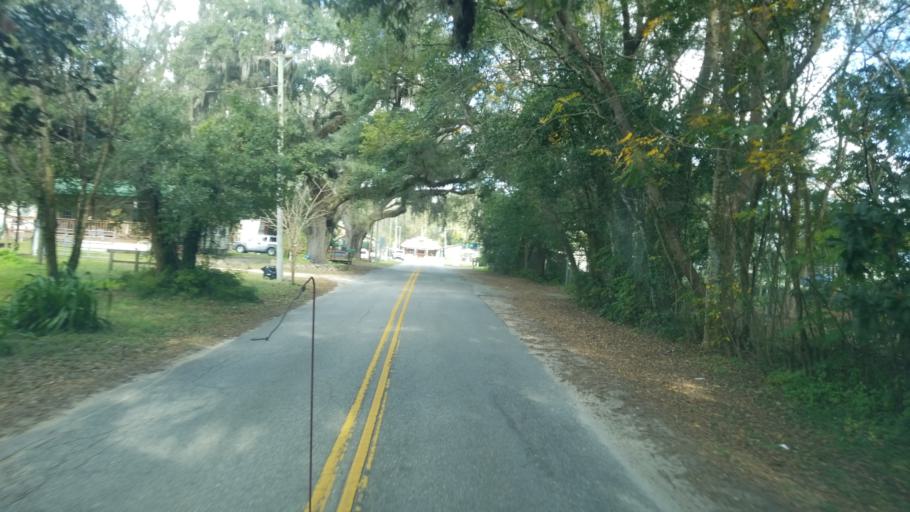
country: US
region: Florida
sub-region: Citrus County
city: Floral City
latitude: 28.7488
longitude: -82.2960
